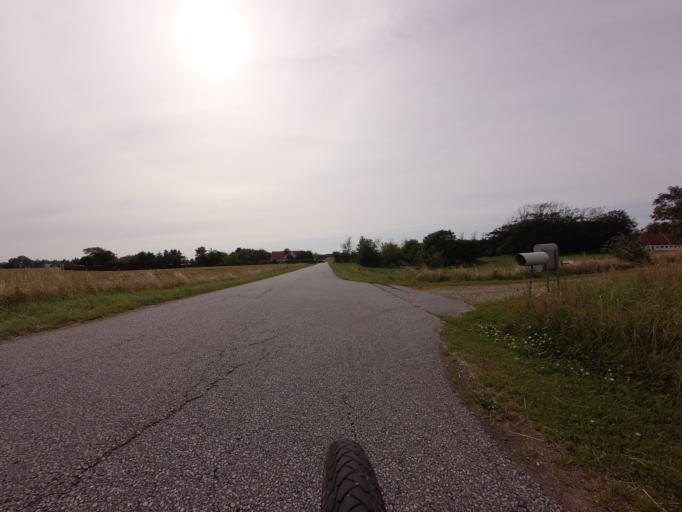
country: DK
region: North Denmark
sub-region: Hjorring Kommune
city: Hjorring
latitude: 57.4336
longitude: 9.8984
